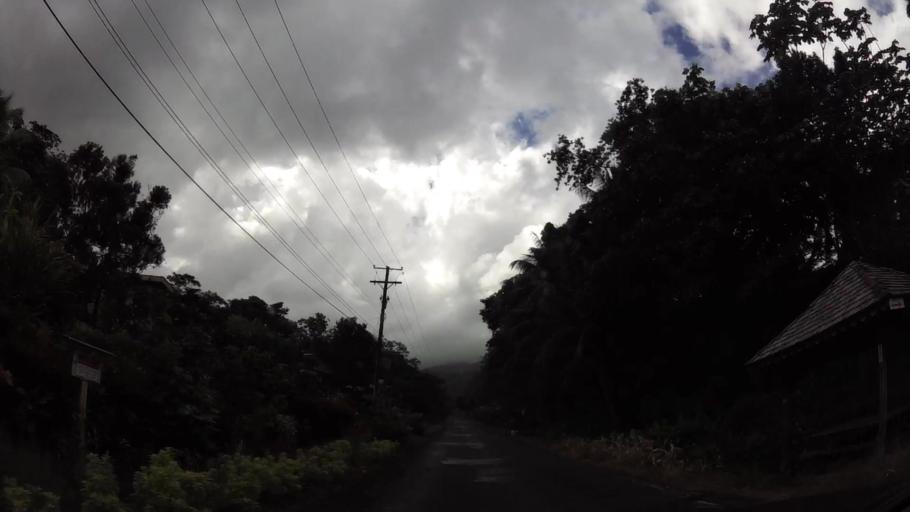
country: DM
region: Saint David
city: Castle Bruce
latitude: 15.4071
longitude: -61.3035
